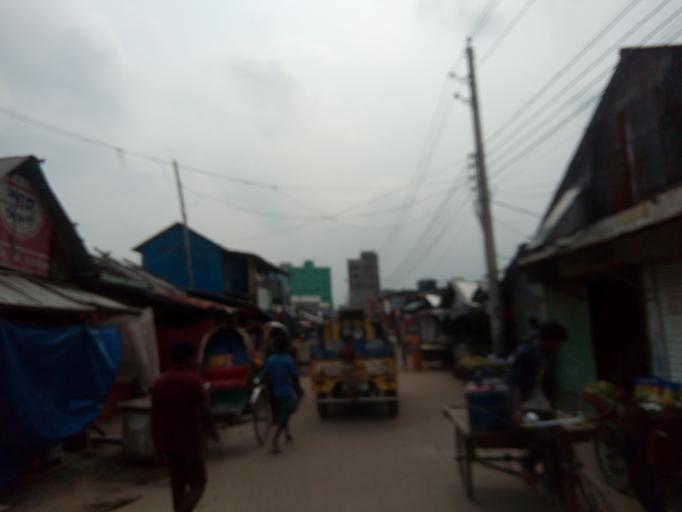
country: BD
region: Dhaka
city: Azimpur
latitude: 23.7373
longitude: 90.3612
